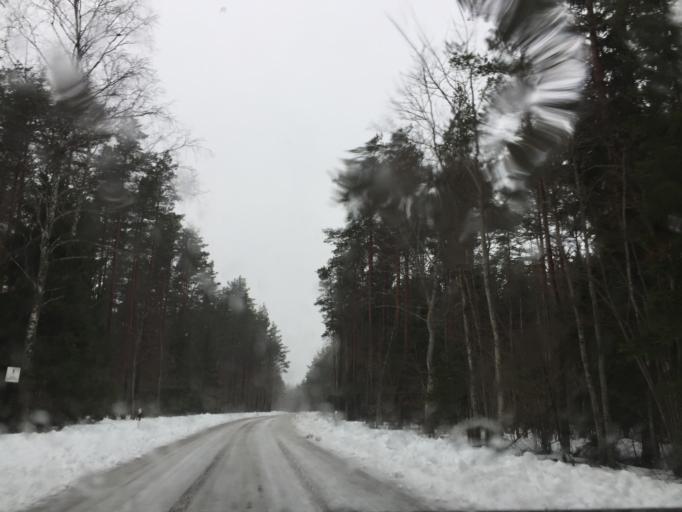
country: EE
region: Saare
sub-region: Kuressaare linn
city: Kuressaare
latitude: 58.2910
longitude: 22.1142
